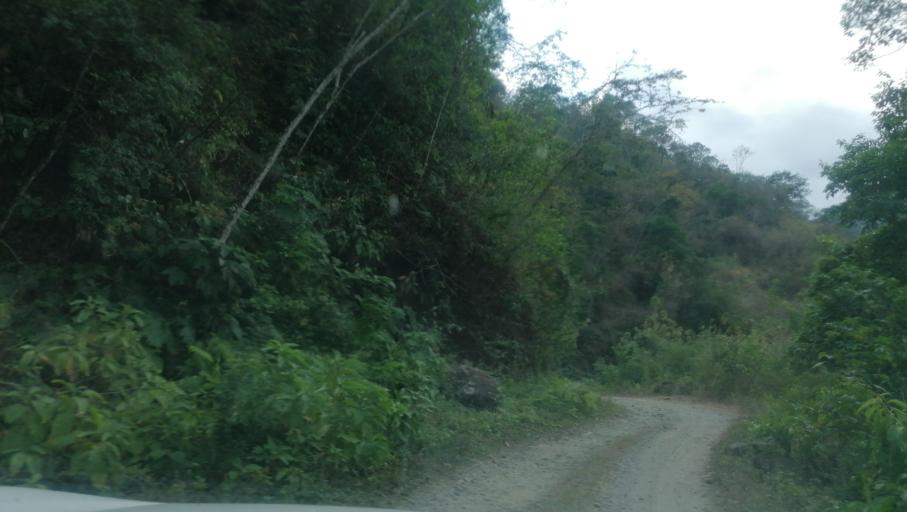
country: MX
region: Chiapas
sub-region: Cacahoatan
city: Benito Juarez
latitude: 15.1585
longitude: -92.1778
